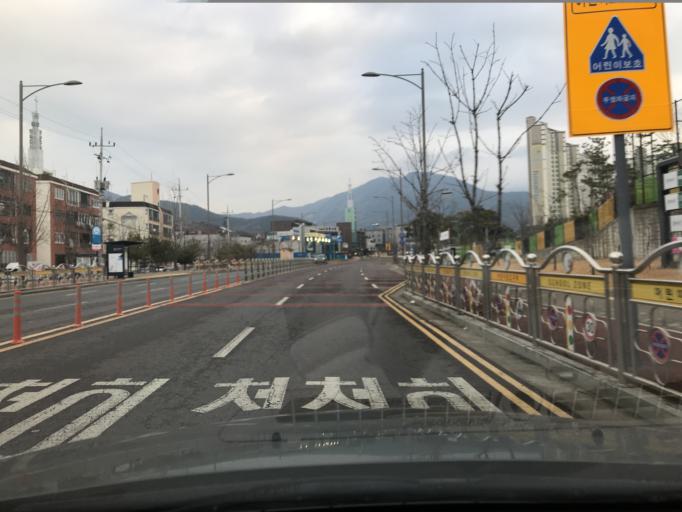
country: KR
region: Daegu
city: Hwawon
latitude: 35.6950
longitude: 128.4512
